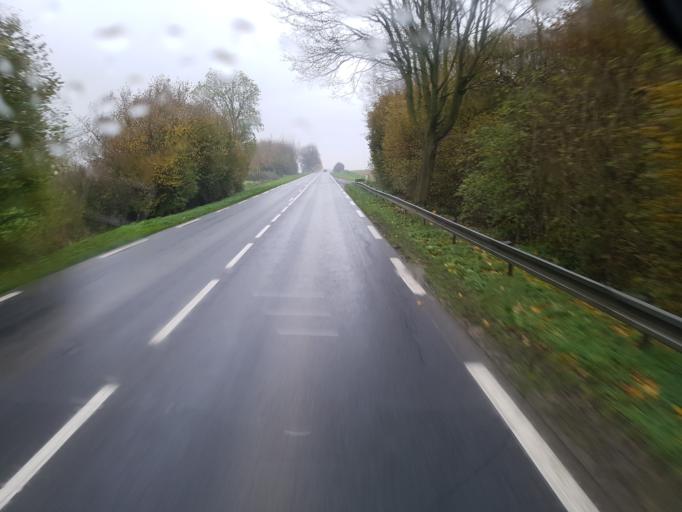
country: FR
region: Picardie
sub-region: Departement de l'Aisne
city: Saint-Quentin
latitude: 49.8845
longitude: 3.2667
